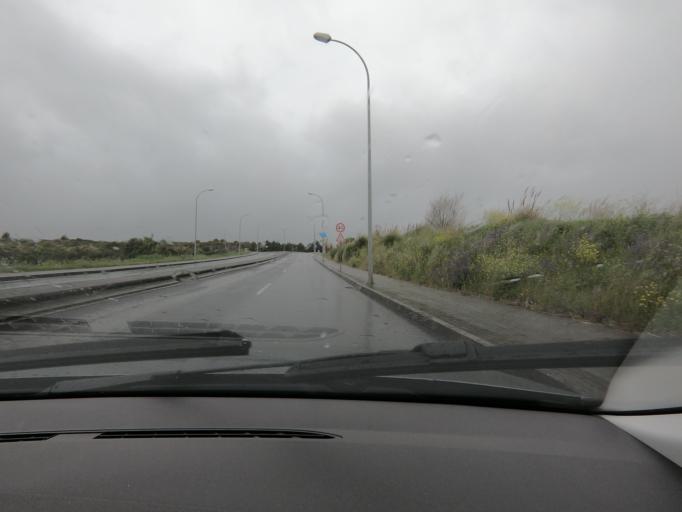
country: PT
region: Lisbon
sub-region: Sintra
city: Sintra
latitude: 38.8023
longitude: -9.3560
